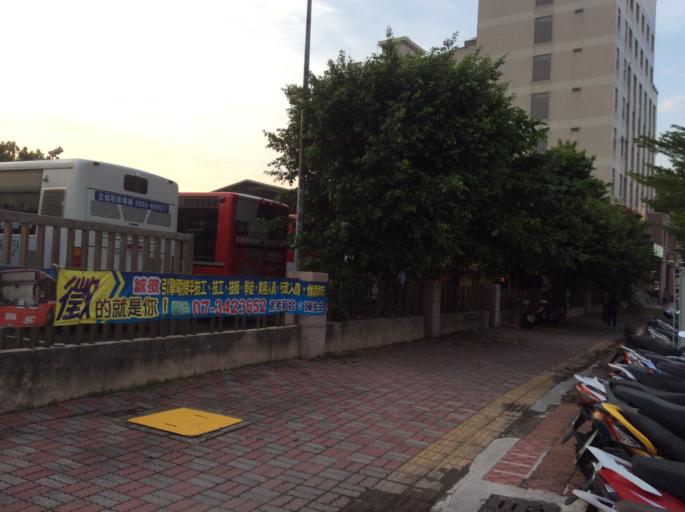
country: TW
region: Kaohsiung
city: Kaohsiung
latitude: 22.6660
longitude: 120.3218
